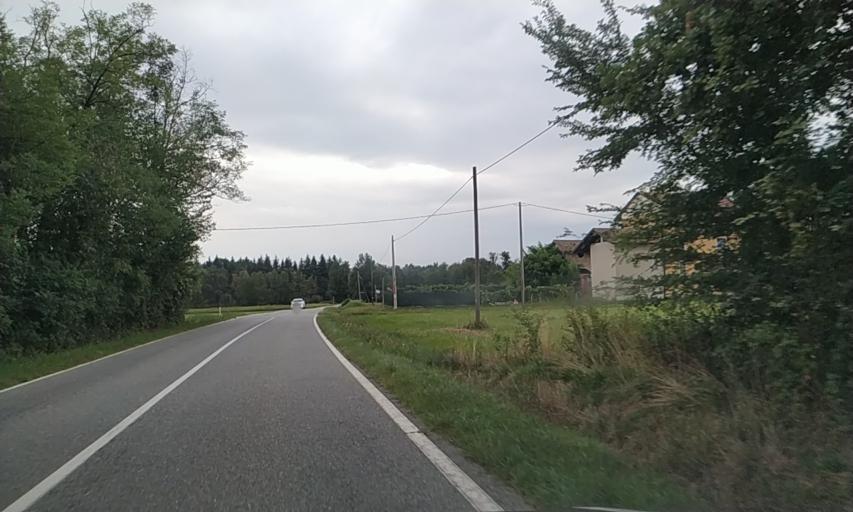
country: IT
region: Piedmont
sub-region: Provincia di Vercelli
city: San Maurizio
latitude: 45.5913
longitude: 8.2937
